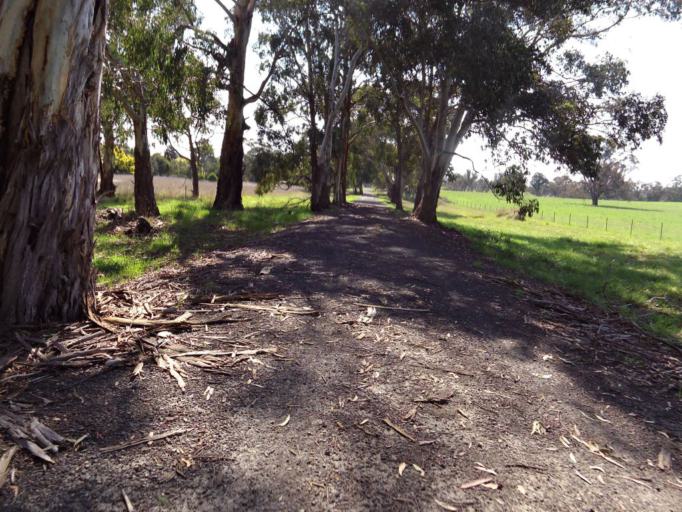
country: AU
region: Victoria
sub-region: Murrindindi
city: Alexandra
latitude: -37.1233
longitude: 145.6004
